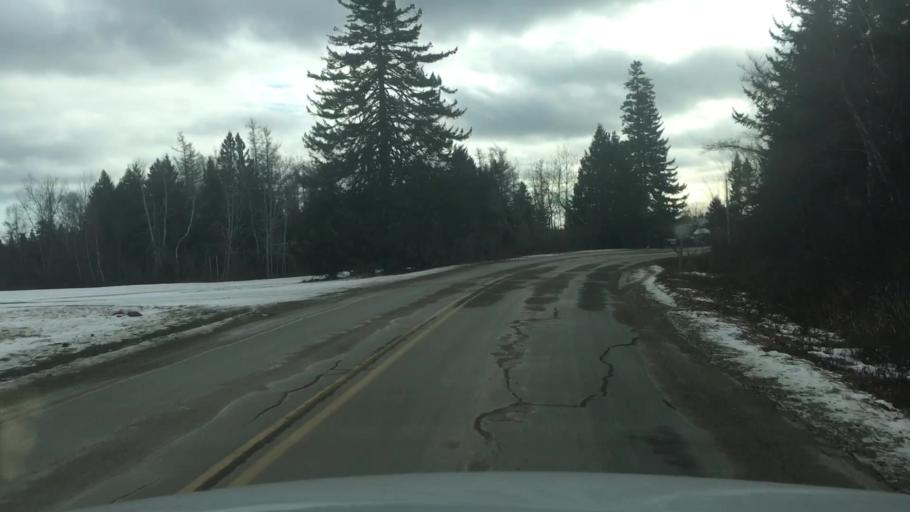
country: US
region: Maine
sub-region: Washington County
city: Machias
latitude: 44.6216
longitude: -67.4788
